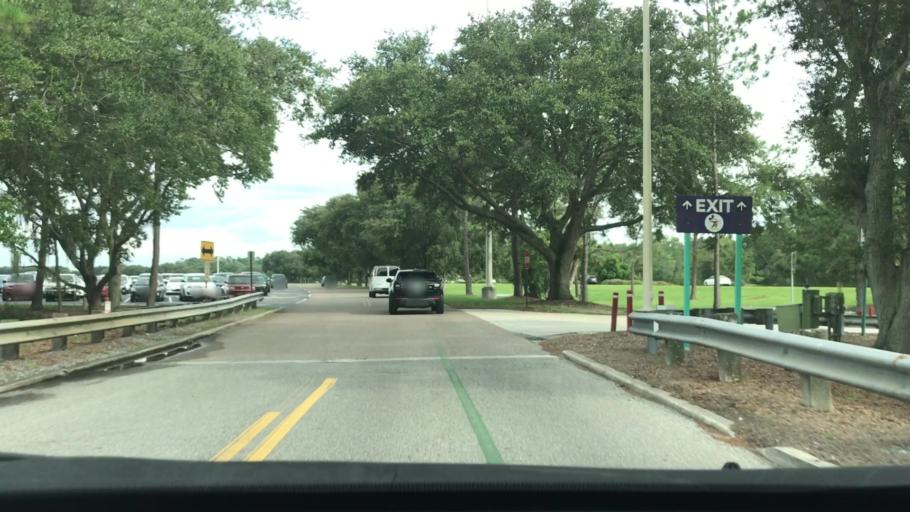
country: US
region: Florida
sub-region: Polk County
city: Citrus Ridge
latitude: 28.3996
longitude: -81.5839
